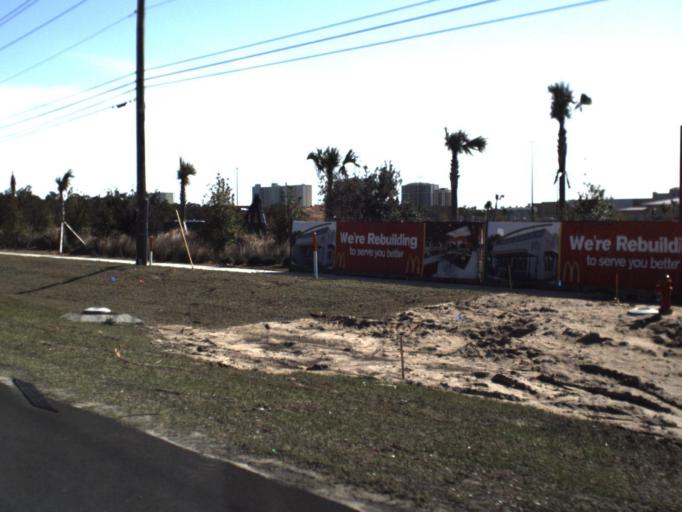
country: US
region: Florida
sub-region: Bay County
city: Laguna Beach
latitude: 30.2205
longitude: -85.8657
